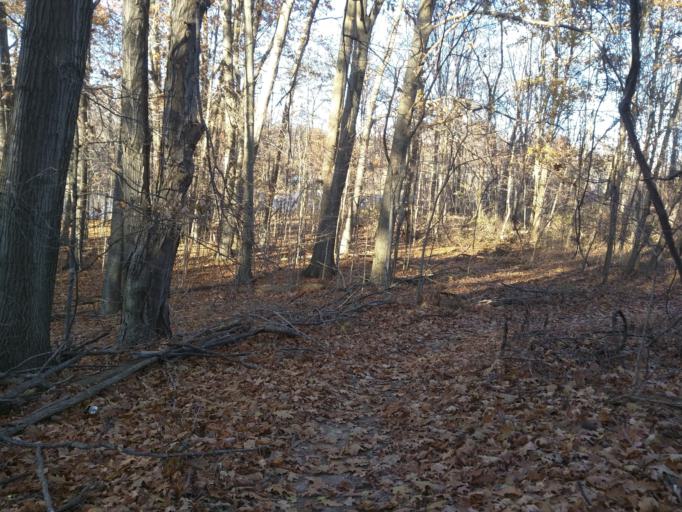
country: US
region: Michigan
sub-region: Eaton County
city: Waverly
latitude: 42.6895
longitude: -84.6185
